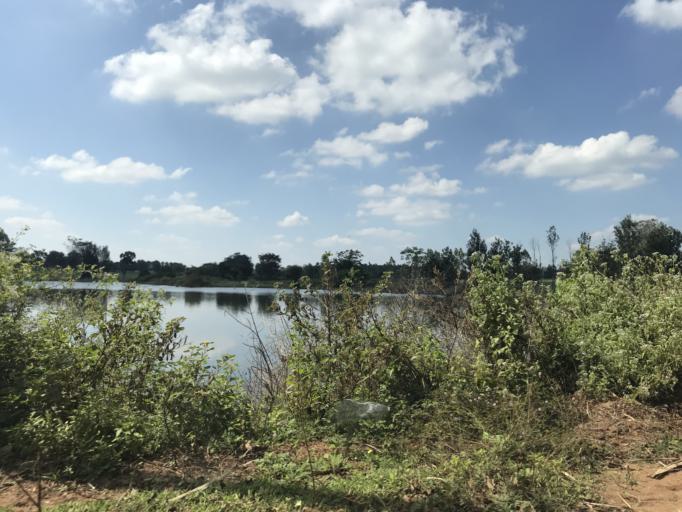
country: IN
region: Karnataka
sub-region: Mysore
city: Heggadadevankote
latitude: 12.1531
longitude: 76.2853
